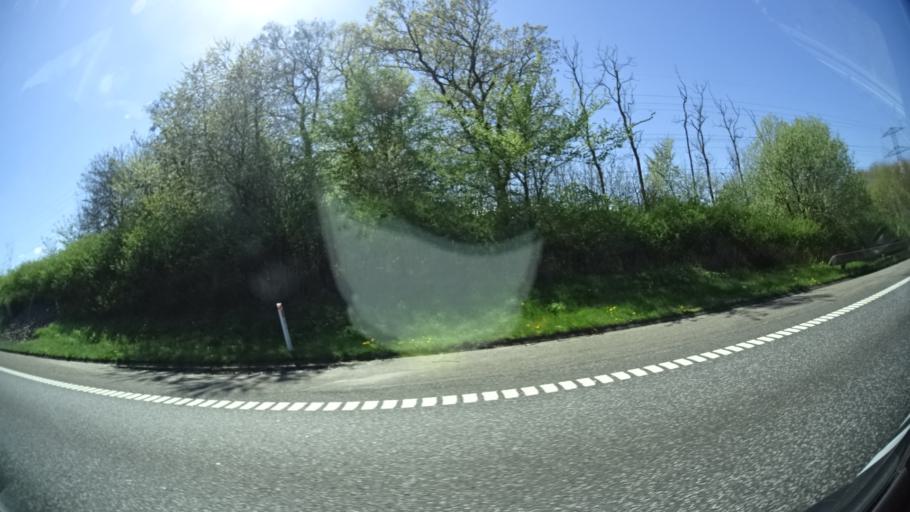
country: DK
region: Central Jutland
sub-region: Arhus Kommune
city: Trige
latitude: 56.2973
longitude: 10.1299
